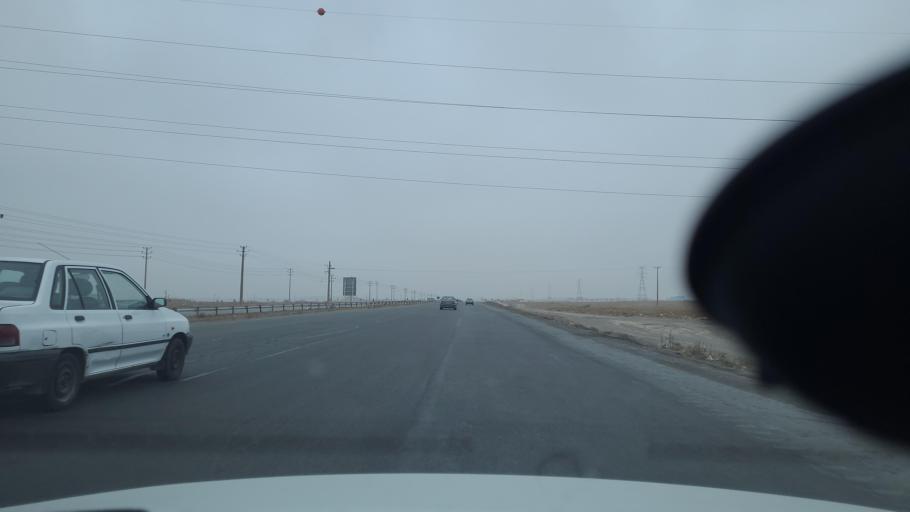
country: IR
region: Razavi Khorasan
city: Fariman
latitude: 35.9412
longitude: 59.7504
